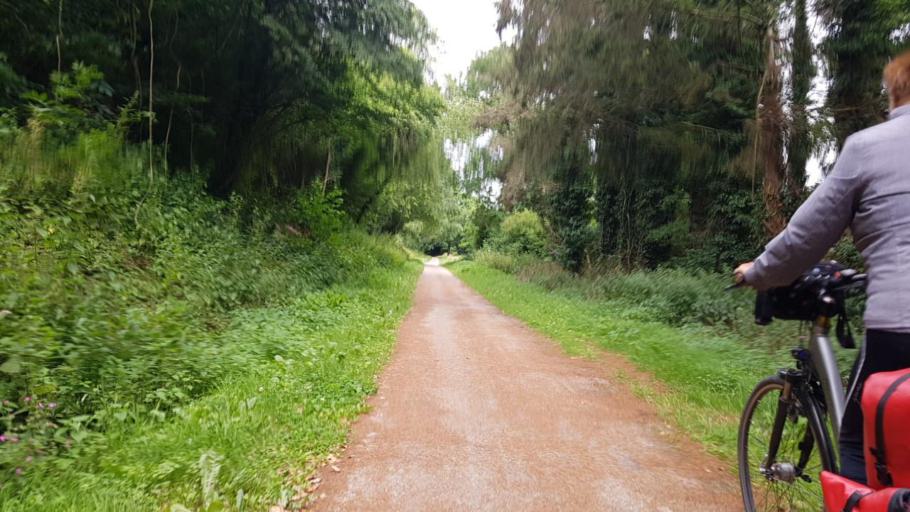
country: FR
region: Picardie
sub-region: Departement de l'Aisne
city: La Capelle
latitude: 49.9059
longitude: 3.9083
